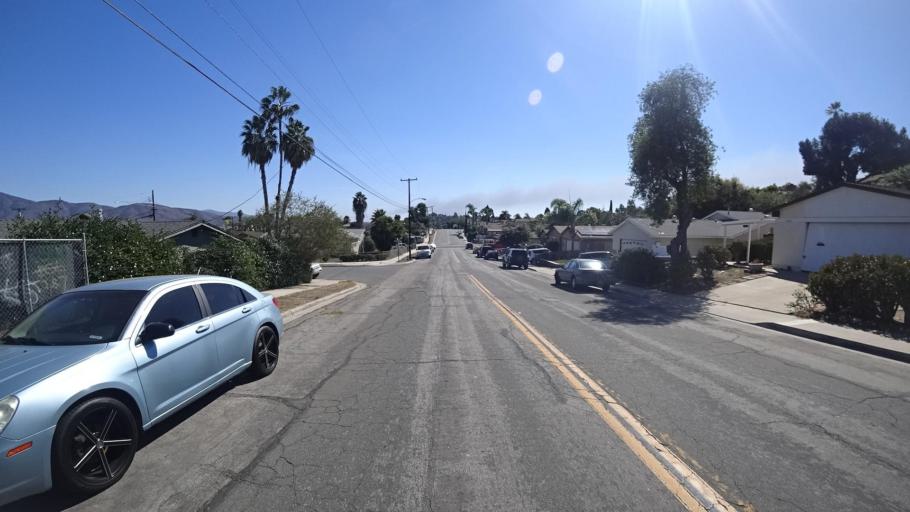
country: US
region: California
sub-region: San Diego County
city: La Presa
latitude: 32.7130
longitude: -117.0198
